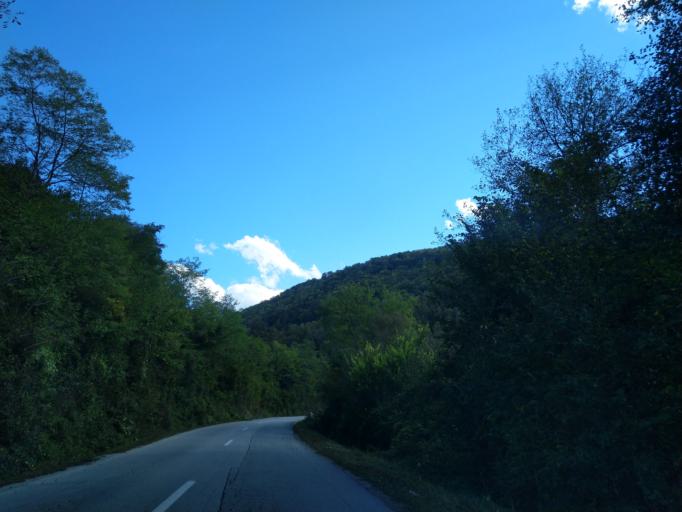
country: RS
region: Central Serbia
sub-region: Zlatiborski Okrug
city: Uzice
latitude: 43.8815
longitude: 19.7784
